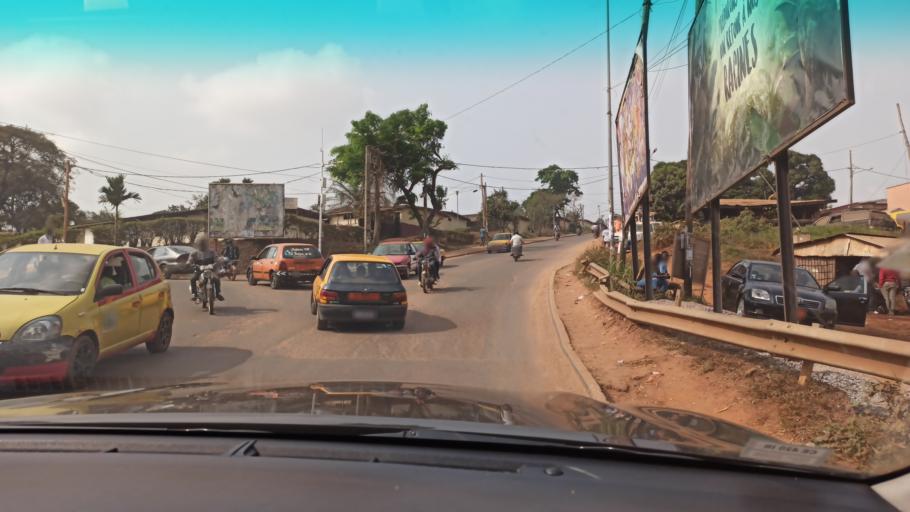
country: CM
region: Centre
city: Yaounde
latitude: 3.8791
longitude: 11.4915
